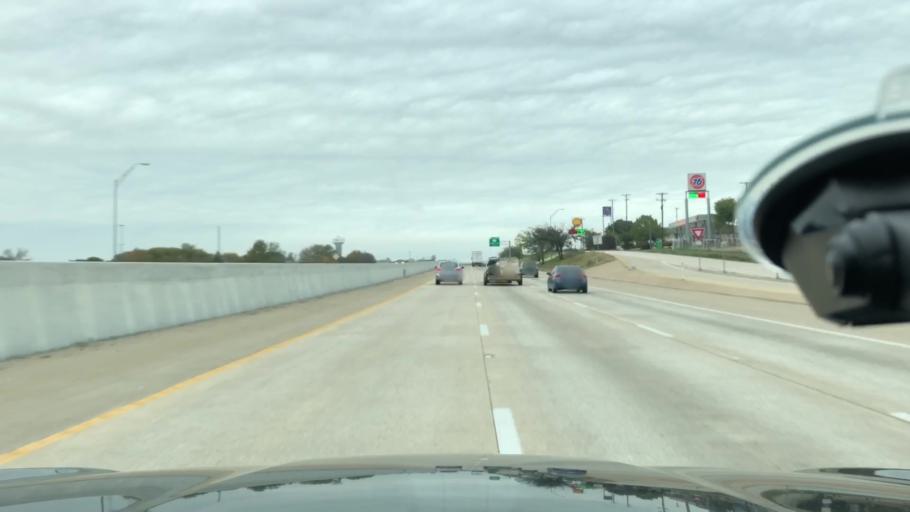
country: US
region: Texas
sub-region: Ellis County
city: Red Oak
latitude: 32.5128
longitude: -96.8221
